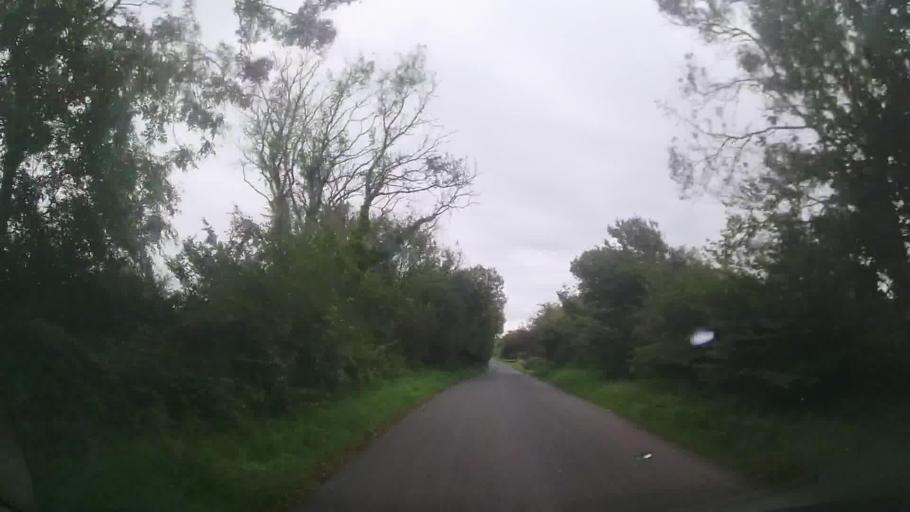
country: GB
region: Wales
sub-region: Carmarthenshire
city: Whitland
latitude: 51.7509
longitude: -4.6007
